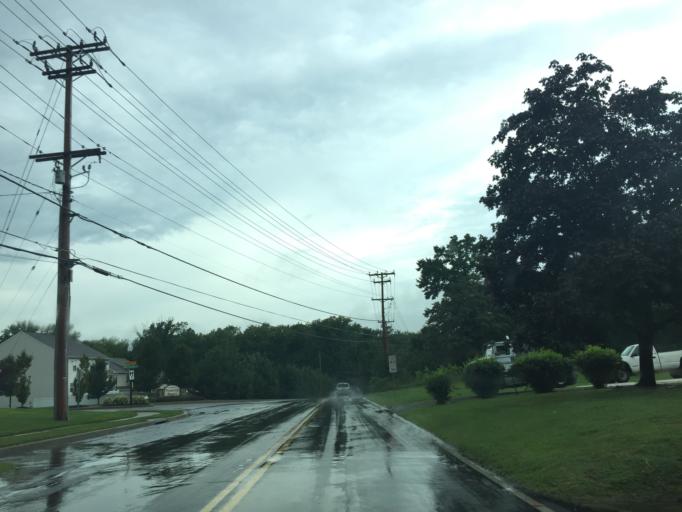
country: US
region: Maryland
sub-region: Harford County
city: Riverside
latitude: 39.4628
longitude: -76.2798
